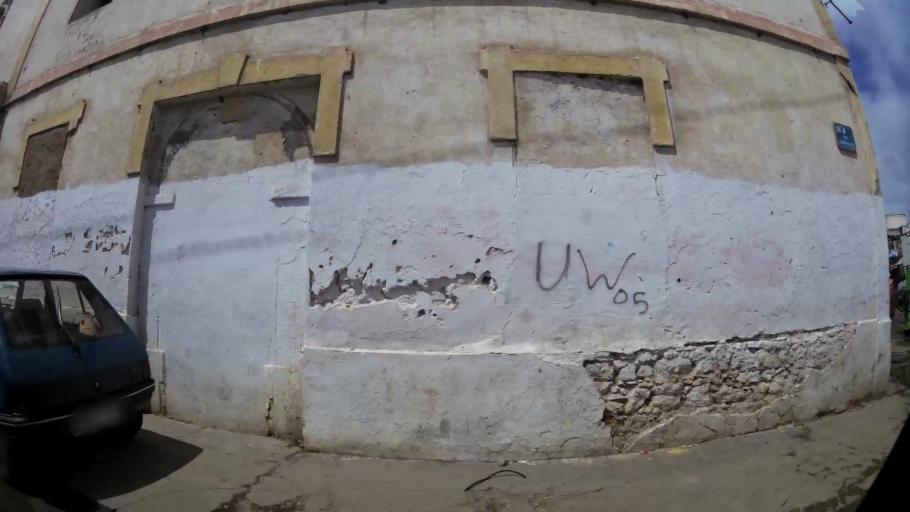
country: MA
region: Grand Casablanca
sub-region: Casablanca
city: Casablanca
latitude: 33.5956
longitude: -7.6227
